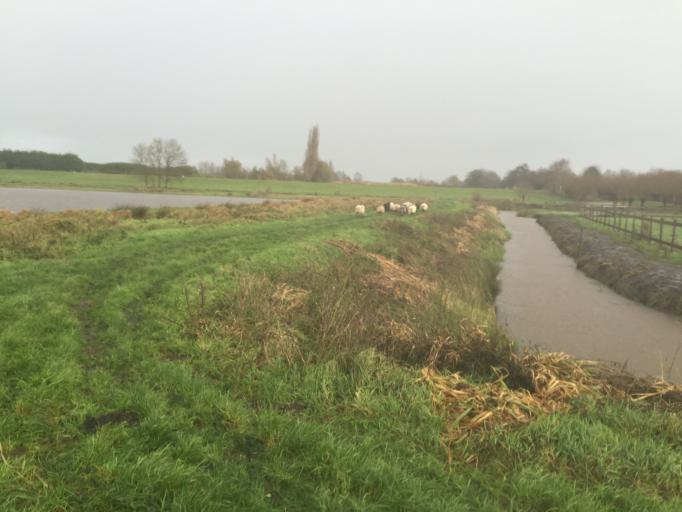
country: NL
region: Utrecht
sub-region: Gemeente De Ronde Venen
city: Mijdrecht
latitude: 52.1820
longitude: 4.8306
